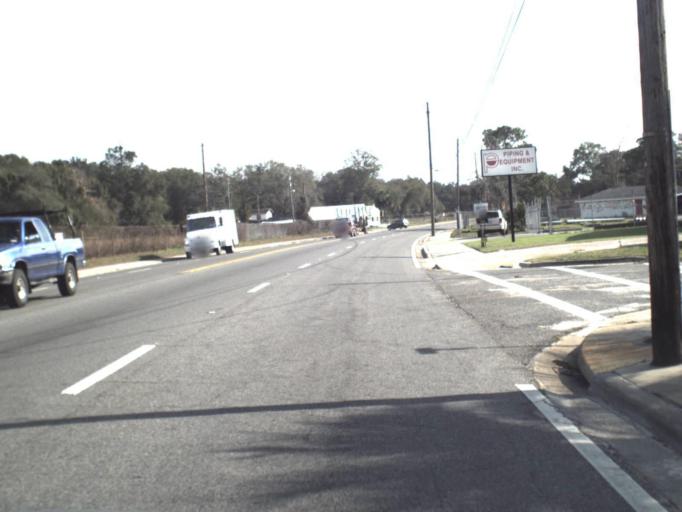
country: US
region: Florida
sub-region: Bay County
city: Springfield
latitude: 30.1515
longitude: -85.6163
